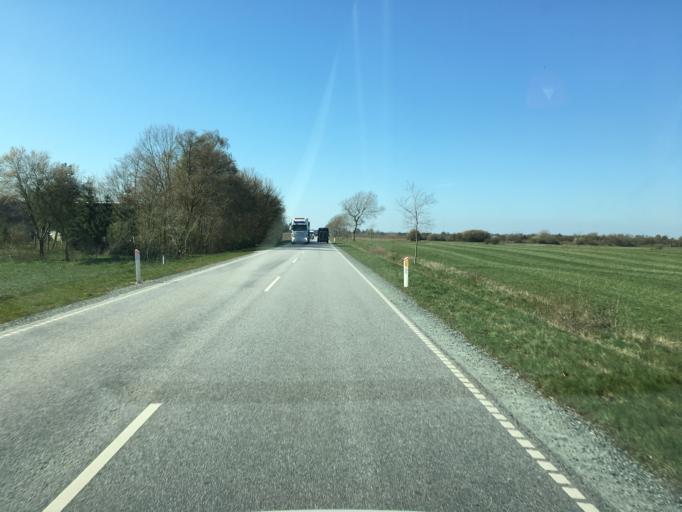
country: DK
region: South Denmark
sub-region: Aabenraa Kommune
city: Tinglev
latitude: 54.9586
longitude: 9.3318
